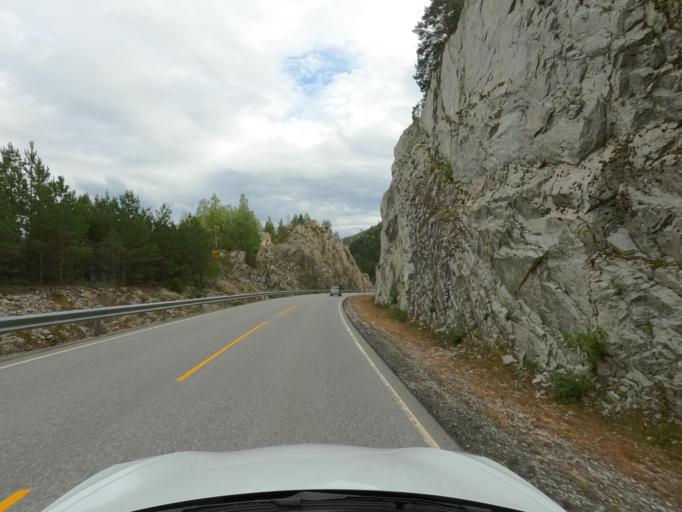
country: NO
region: Telemark
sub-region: Hjartdal
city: Sauland
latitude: 59.7943
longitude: 9.0009
